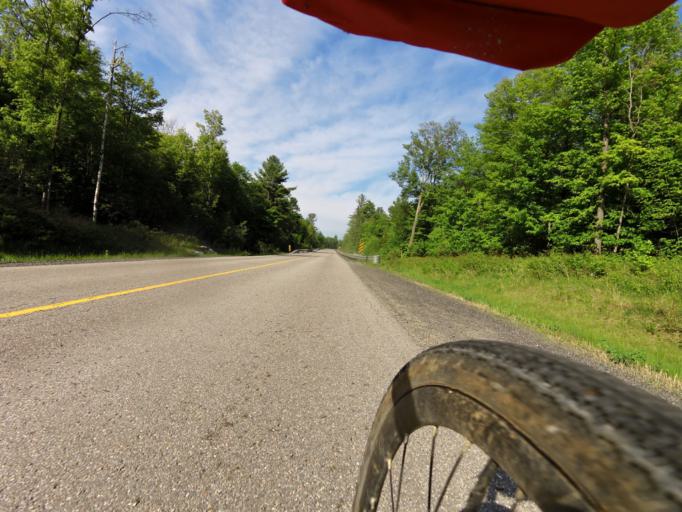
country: CA
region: Ontario
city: Arnprior
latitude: 45.1676
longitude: -76.4966
